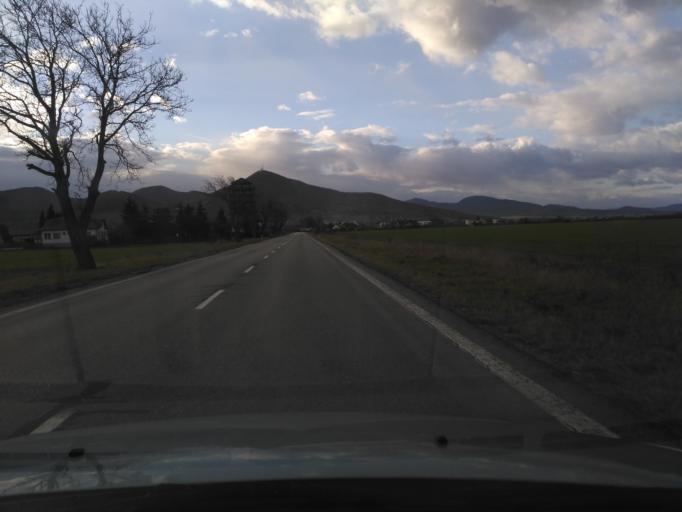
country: HU
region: Borsod-Abauj-Zemplen
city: Satoraljaujhely
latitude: 48.3974
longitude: 21.6871
